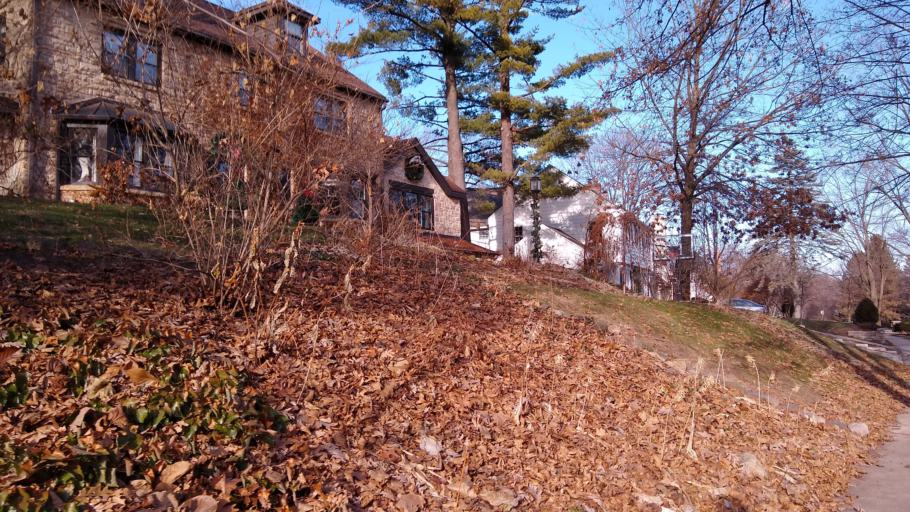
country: US
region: Wisconsin
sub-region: Dane County
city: Shorewood Hills
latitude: 43.0417
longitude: -89.4417
